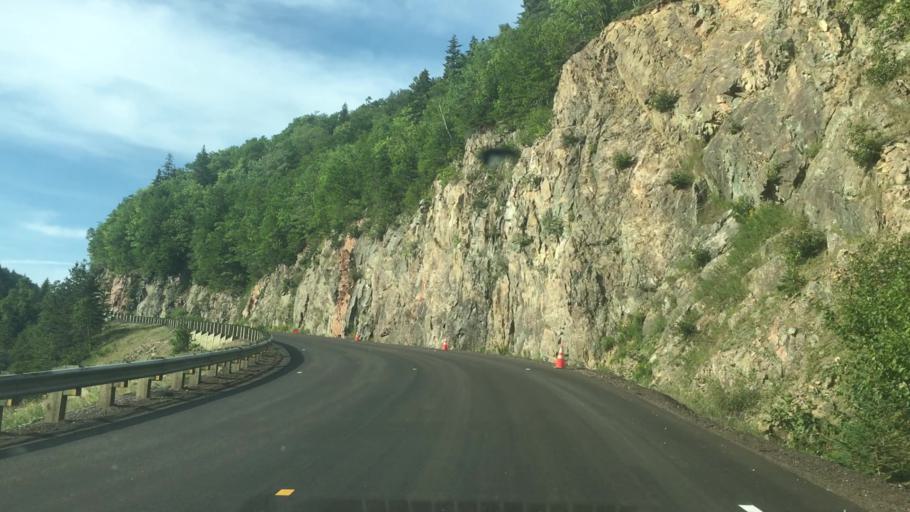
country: CA
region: Nova Scotia
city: Sydney Mines
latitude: 46.8171
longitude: -60.6511
